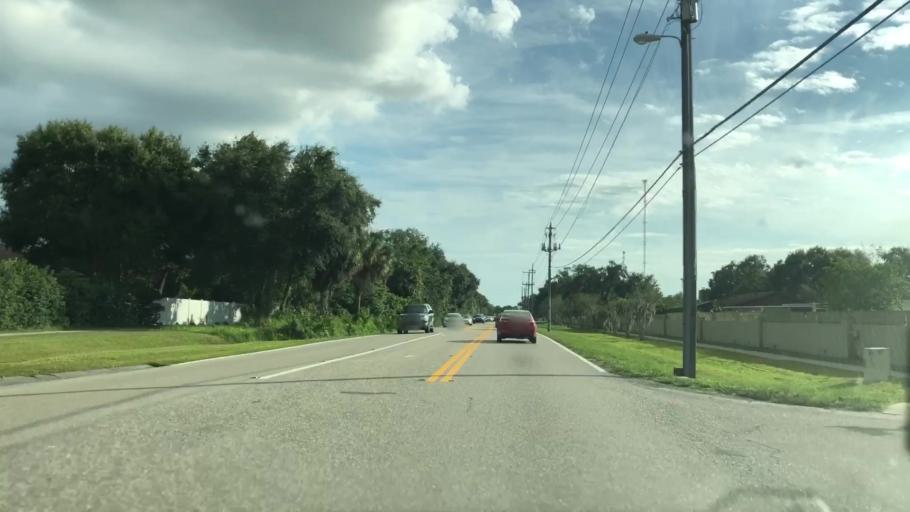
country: US
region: Florida
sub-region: Sarasota County
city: The Meadows
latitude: 27.3476
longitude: -82.4639
